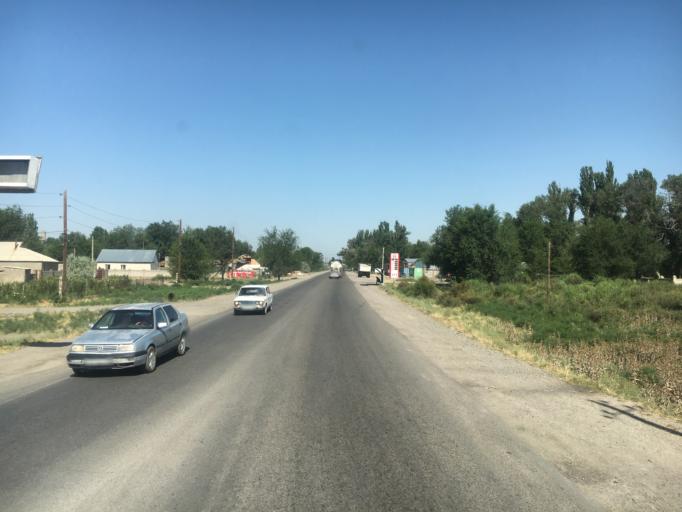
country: KZ
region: Zhambyl
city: Taraz
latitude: 42.9427
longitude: 71.4139
